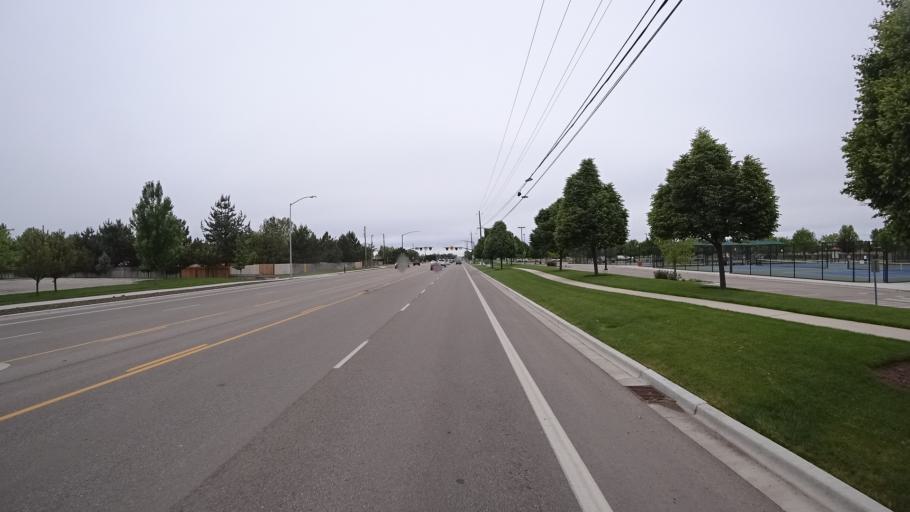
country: US
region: Idaho
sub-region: Ada County
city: Meridian
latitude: 43.6339
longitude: -116.3965
